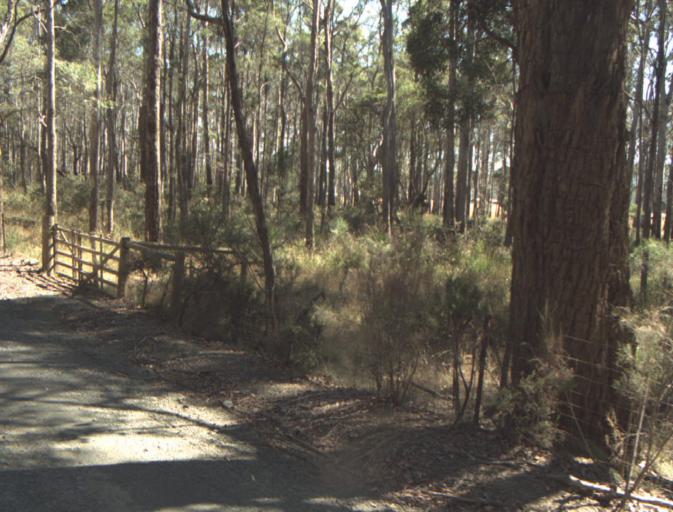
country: AU
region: Tasmania
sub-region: Launceston
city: Newstead
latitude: -41.3575
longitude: 147.2253
